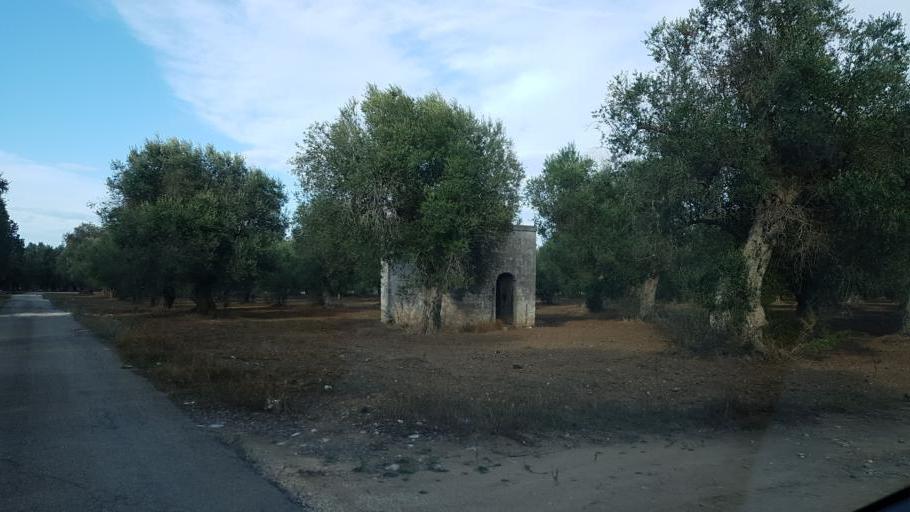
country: IT
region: Apulia
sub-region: Provincia di Brindisi
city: Oria
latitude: 40.5041
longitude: 17.6715
